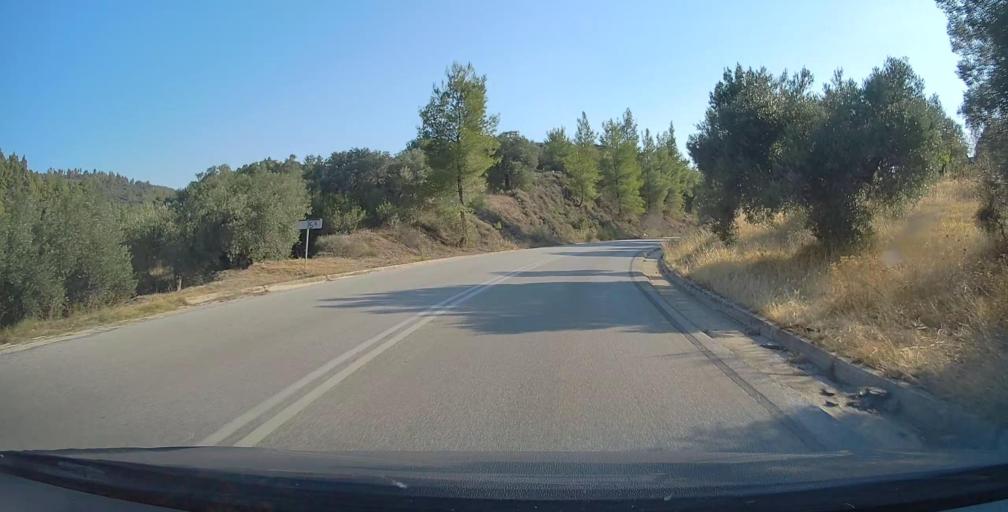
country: GR
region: Central Macedonia
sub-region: Nomos Chalkidikis
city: Neos Marmaras
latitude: 40.0833
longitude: 23.8090
